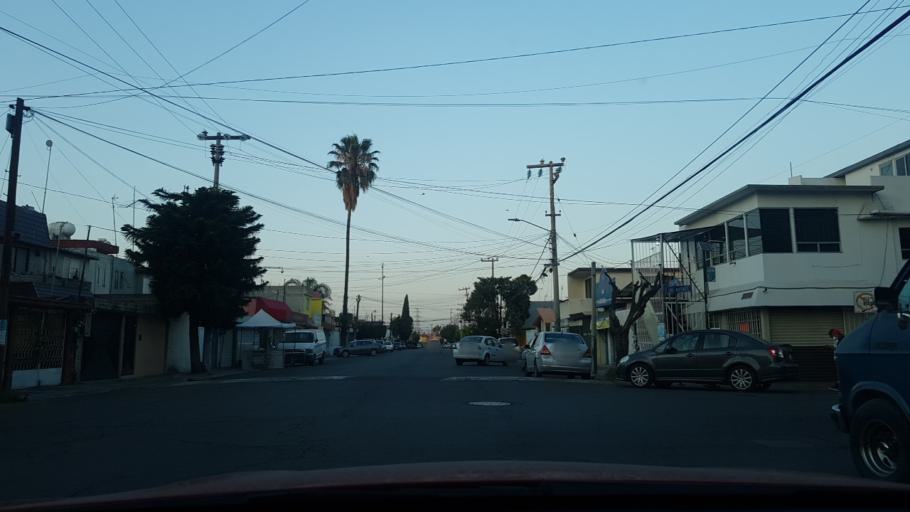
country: MX
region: Mexico
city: Cuautitlan
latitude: 19.6864
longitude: -99.2063
